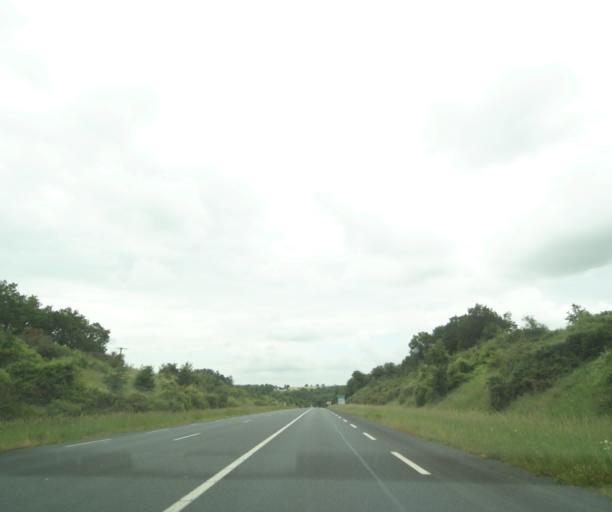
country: FR
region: Poitou-Charentes
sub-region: Departement des Deux-Sevres
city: Saint-Varent
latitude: 46.9107
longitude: -0.1938
